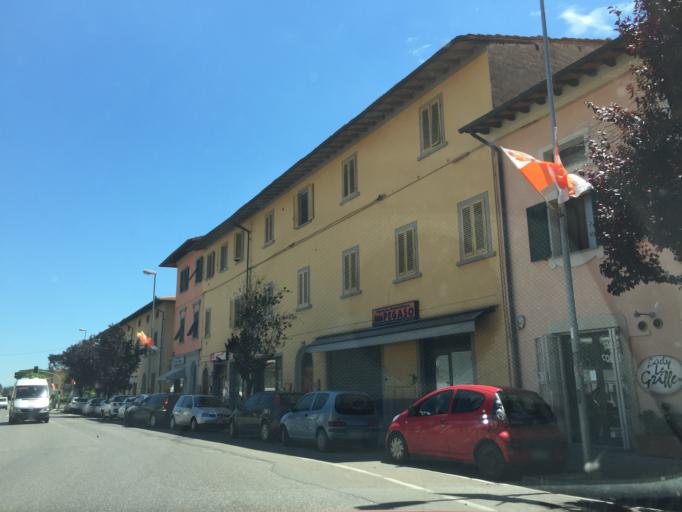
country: IT
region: Tuscany
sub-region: Province of Pisa
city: San Miniato
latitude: 43.6860
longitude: 10.7917
